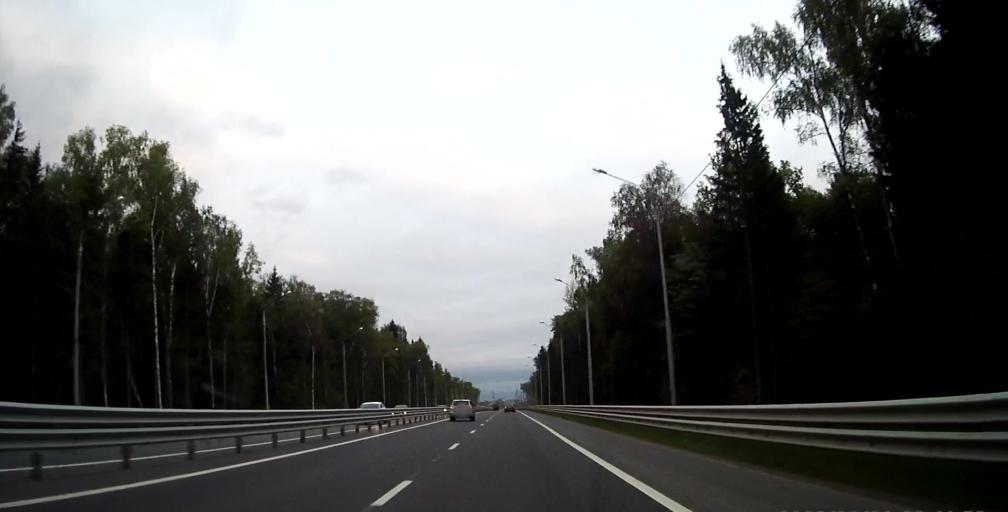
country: RU
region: Moskovskaya
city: Klimovsk
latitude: 55.3948
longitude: 37.5029
